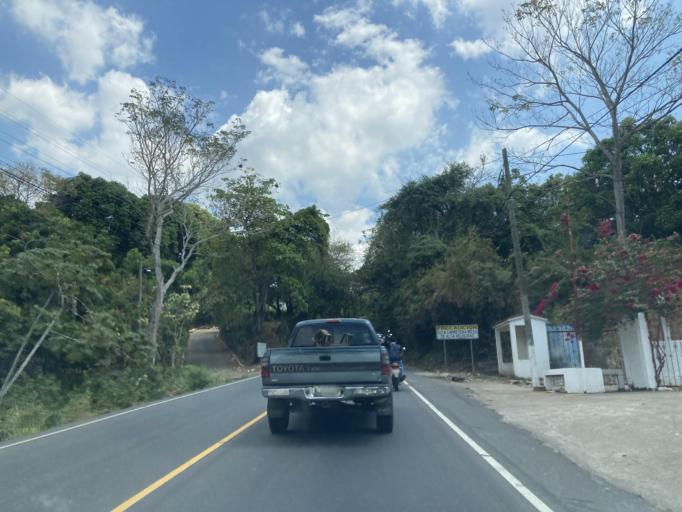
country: GT
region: Santa Rosa
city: Guazacapan
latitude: 14.0687
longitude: -90.4354
